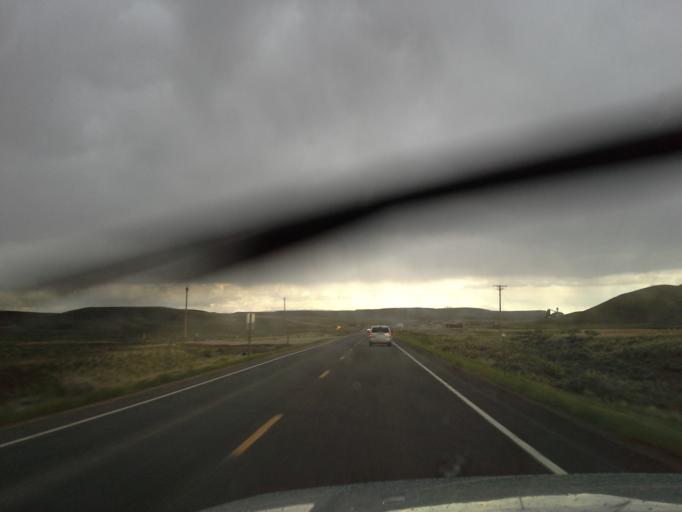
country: US
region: Wyoming
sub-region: Park County
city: Powell
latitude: 45.0647
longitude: -108.6678
